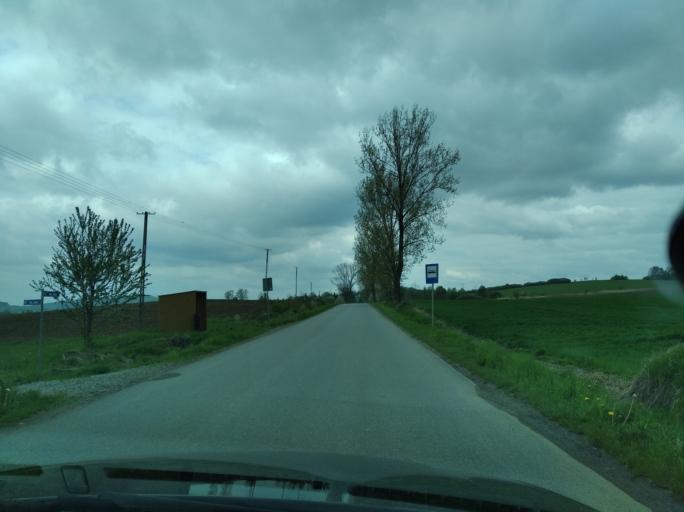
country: PL
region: Subcarpathian Voivodeship
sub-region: Powiat brzozowski
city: Turze Pole
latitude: 49.6285
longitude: 22.0094
